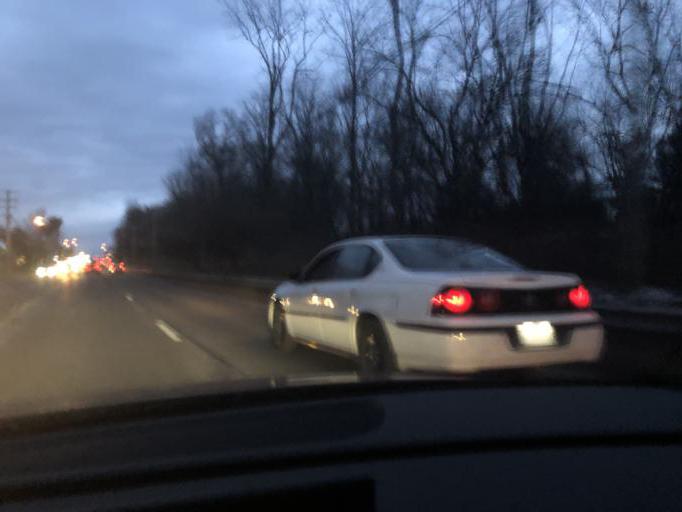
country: US
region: New Jersey
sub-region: Morris County
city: Florham Park
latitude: 40.7895
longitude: -74.4016
